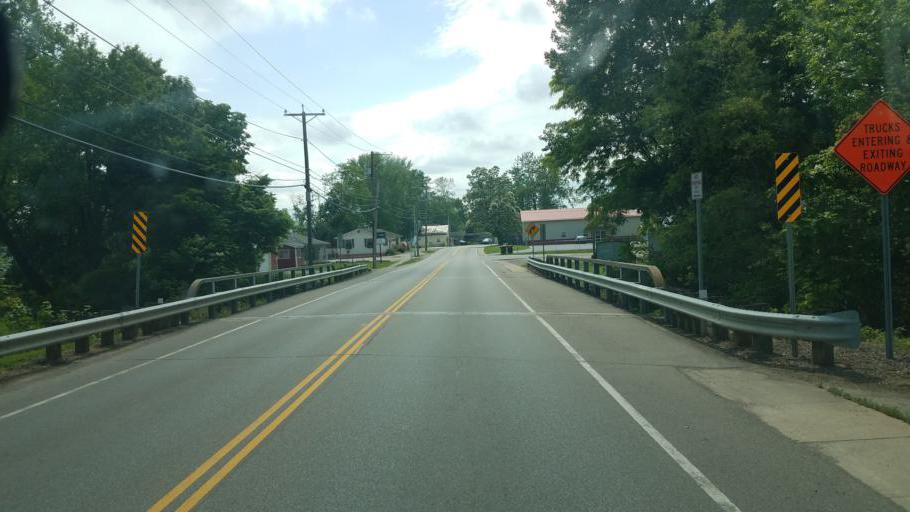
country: US
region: Ohio
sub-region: Licking County
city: Buckeye Lake
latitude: 39.9292
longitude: -82.4865
